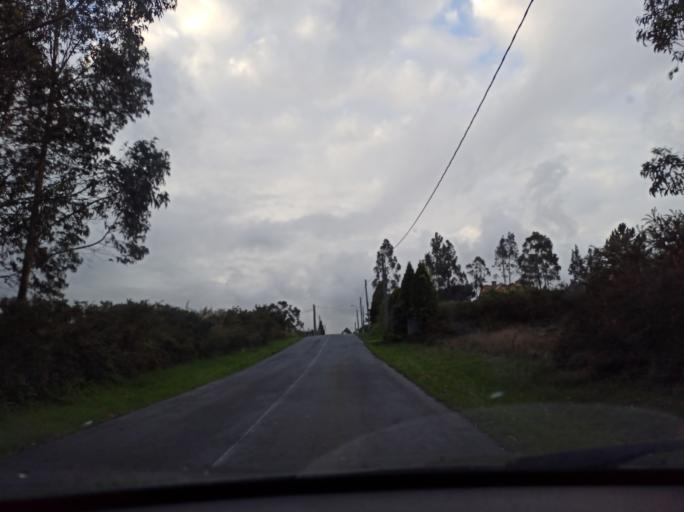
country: ES
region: Galicia
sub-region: Provincia da Coruna
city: Culleredo
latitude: 43.2969
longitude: -8.4305
